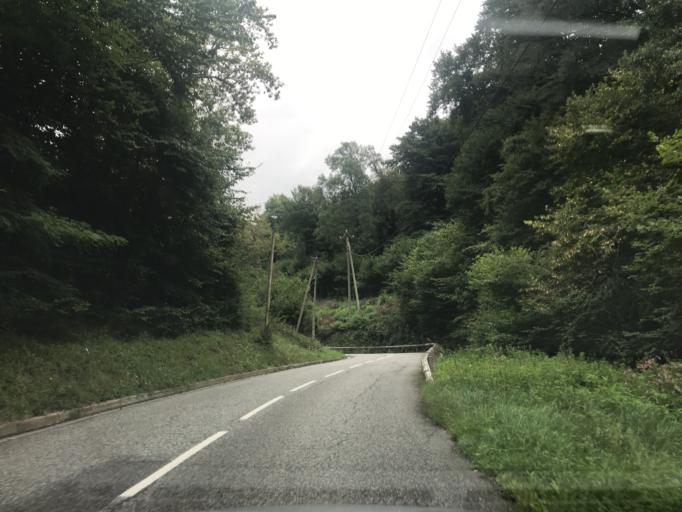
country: FR
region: Midi-Pyrenees
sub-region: Departement de la Haute-Garonne
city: Bagneres-de-Luchon
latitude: 42.7687
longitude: 0.6187
